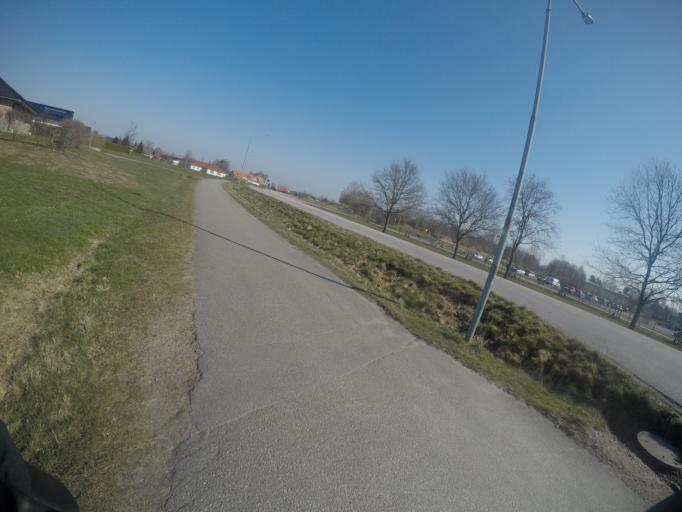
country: SE
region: Halland
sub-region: Laholms Kommun
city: Laholm
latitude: 56.5032
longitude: 13.0505
